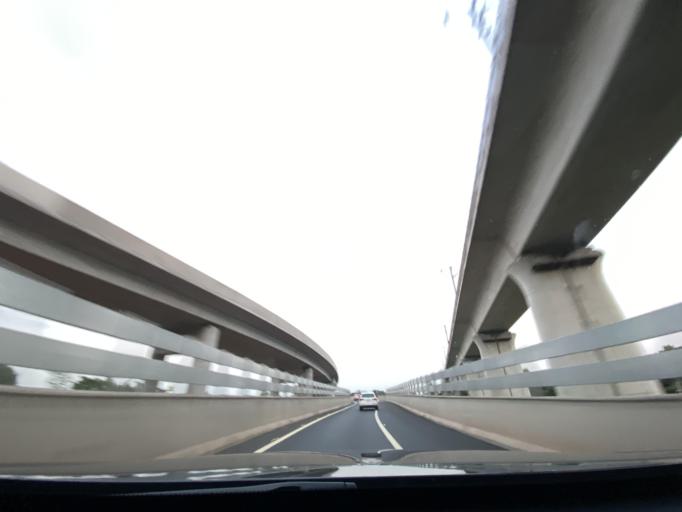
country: CN
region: Sichuan
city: Chengdu
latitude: 30.5716
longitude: 104.1361
